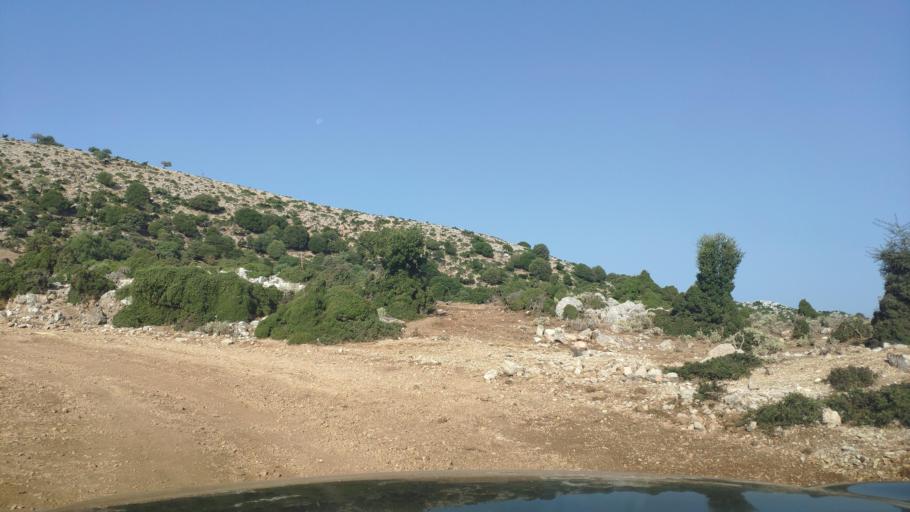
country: GR
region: West Greece
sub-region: Nomos Aitolias kai Akarnanias
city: Monastirakion
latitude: 38.8295
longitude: 20.9773
